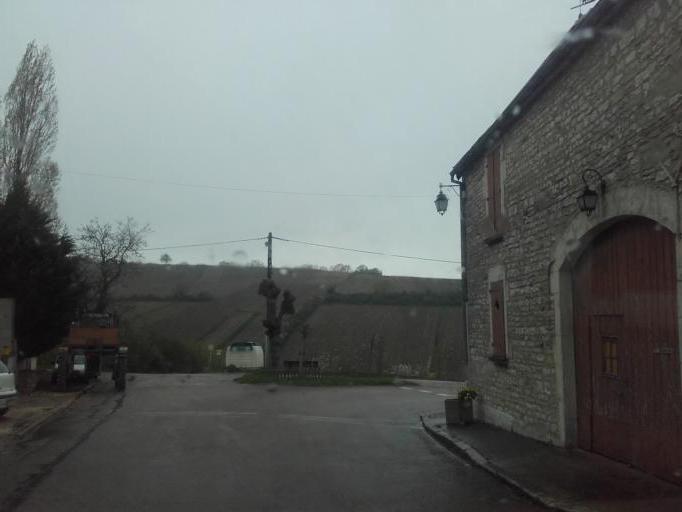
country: FR
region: Bourgogne
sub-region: Departement de l'Yonne
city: Chablis
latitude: 47.7755
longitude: 3.7548
